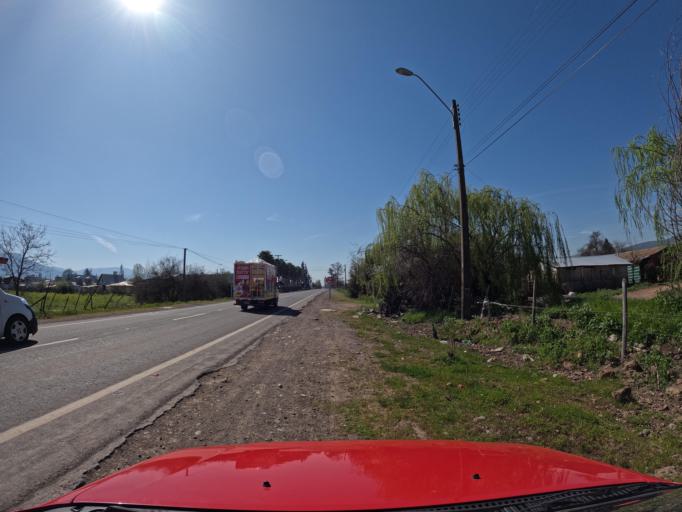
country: CL
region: Maule
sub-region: Provincia de Curico
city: Rauco
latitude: -35.0400
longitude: -71.4539
